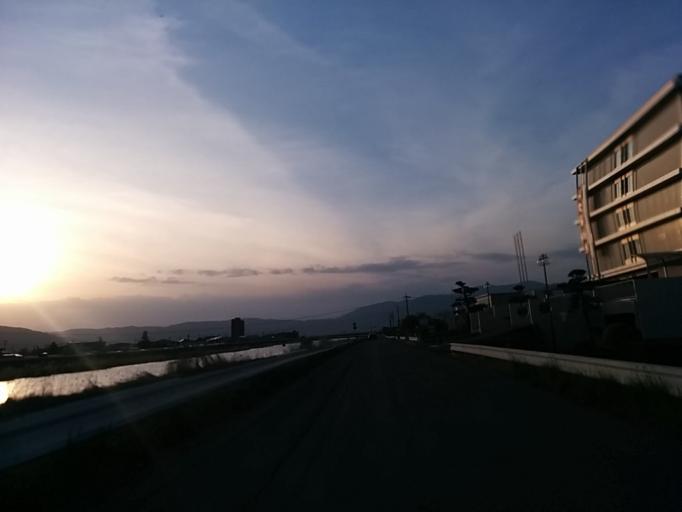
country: JP
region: Nagano
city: Suwa
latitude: 36.0332
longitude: 138.1075
